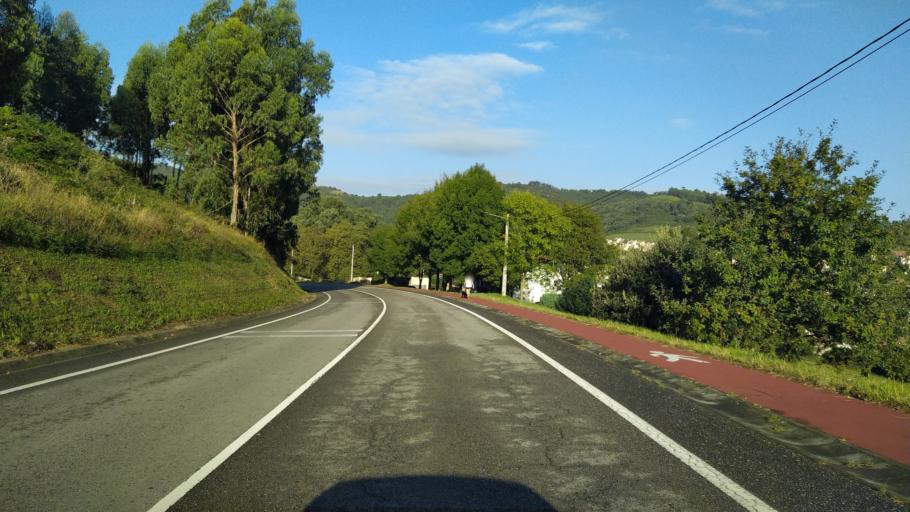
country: ES
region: Cantabria
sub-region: Provincia de Cantabria
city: Santa Cruz de Bezana
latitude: 43.4406
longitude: -3.9242
